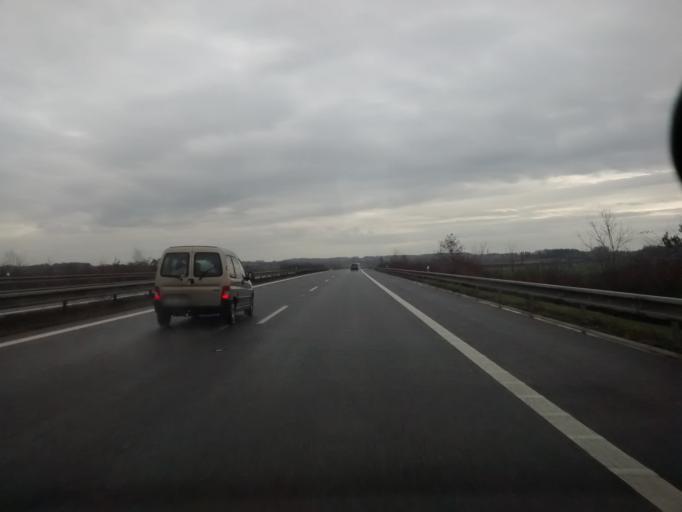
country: CZ
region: Ustecky
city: Roudnice nad Labem
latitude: 50.3633
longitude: 14.2636
